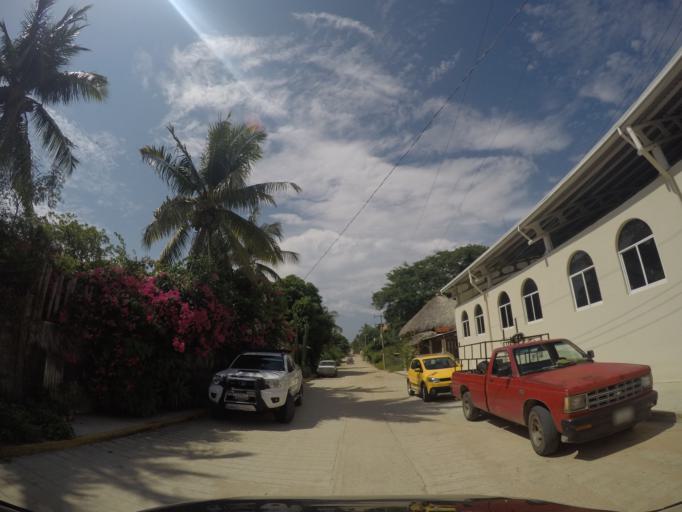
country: MX
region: Oaxaca
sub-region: Santa Maria Colotepec
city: Brisas de Zicatela
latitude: 15.8329
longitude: -97.0426
